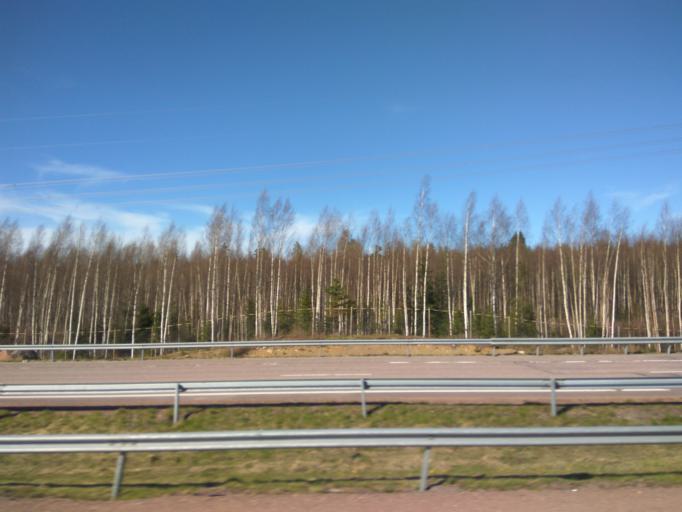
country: FI
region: Uusimaa
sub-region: Loviisa
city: Ruotsinpyhtaeae
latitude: 60.4889
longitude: 26.3504
